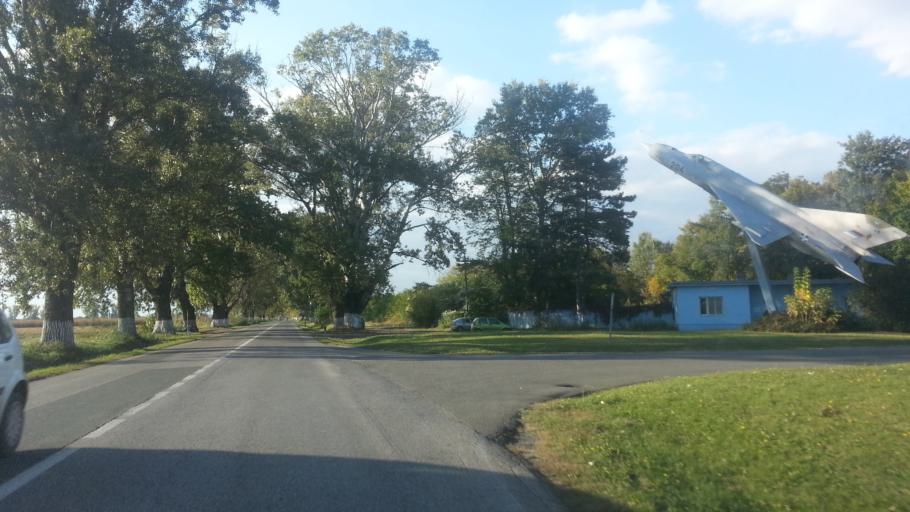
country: RS
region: Autonomna Pokrajina Vojvodina
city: Nova Pazova
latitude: 44.9267
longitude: 20.2450
